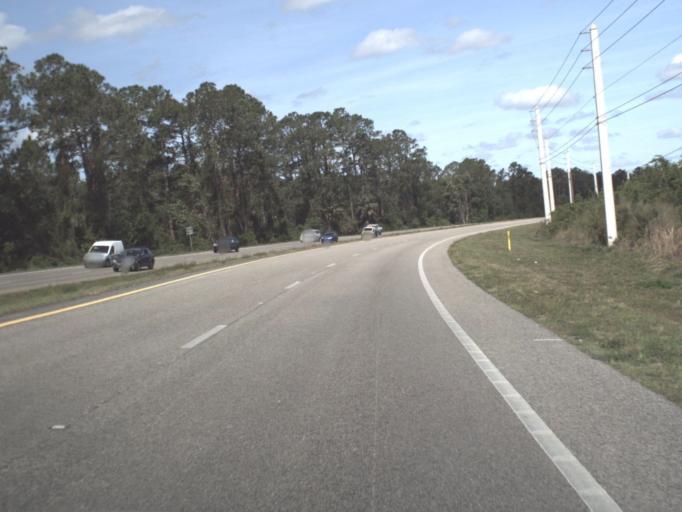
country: US
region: Florida
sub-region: Flagler County
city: Bunnell
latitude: 29.4097
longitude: -81.2018
